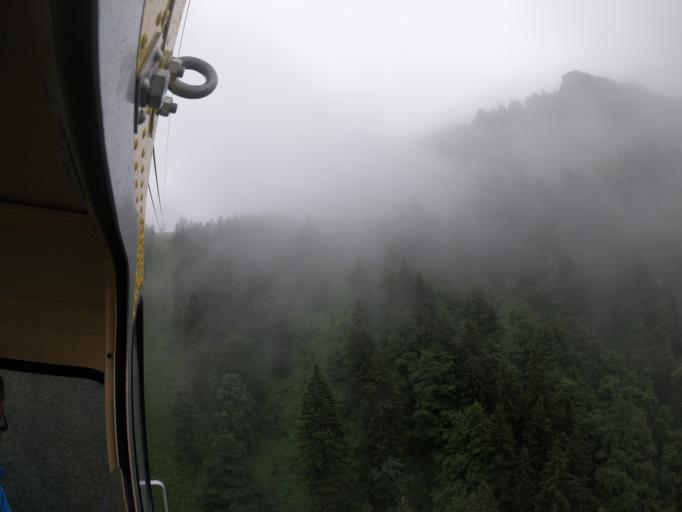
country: DE
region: Bavaria
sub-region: Upper Bavaria
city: Aschau im Chiemgau
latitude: 47.7551
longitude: 12.3468
